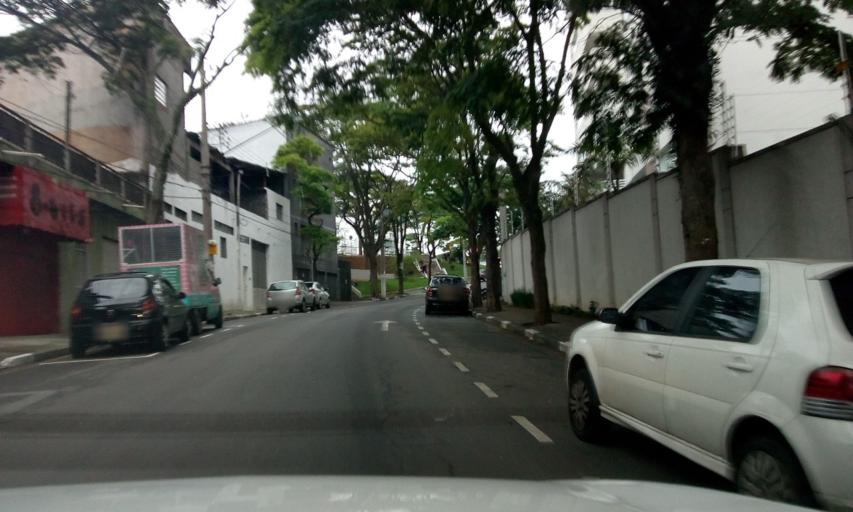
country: BR
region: Sao Paulo
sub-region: Diadema
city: Diadema
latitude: -23.6891
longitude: -46.6162
